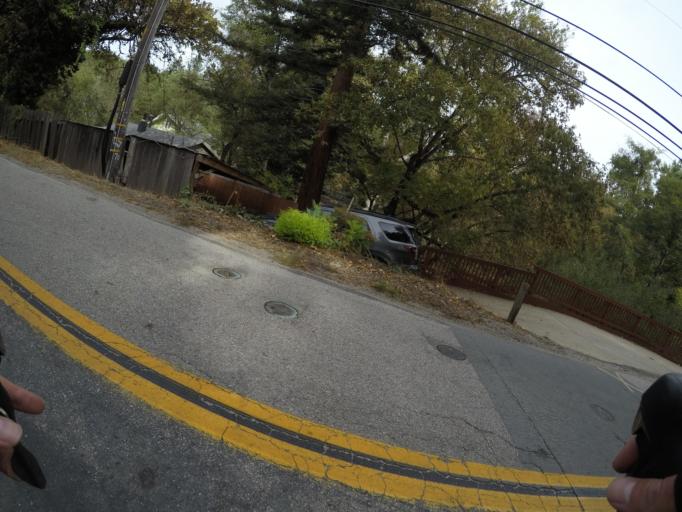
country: US
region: California
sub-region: Santa Cruz County
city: Mount Hermon
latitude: 37.0655
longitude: -122.0578
